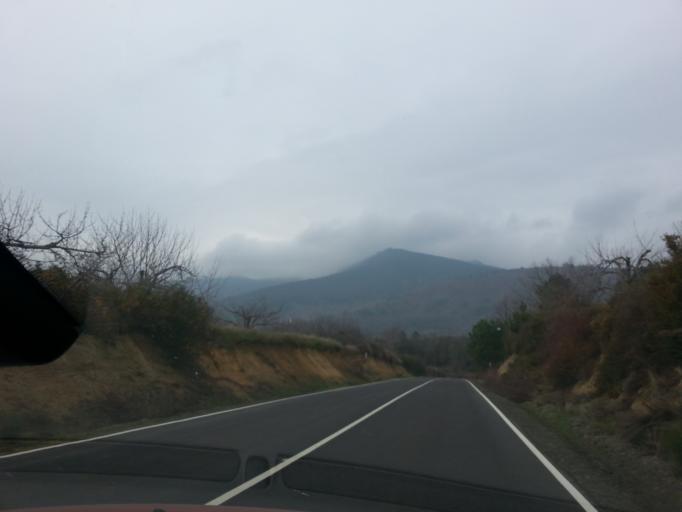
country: ES
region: Castille and Leon
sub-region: Provincia de Salamanca
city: Herguijuela de la Sierra
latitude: 40.4484
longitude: -6.0610
